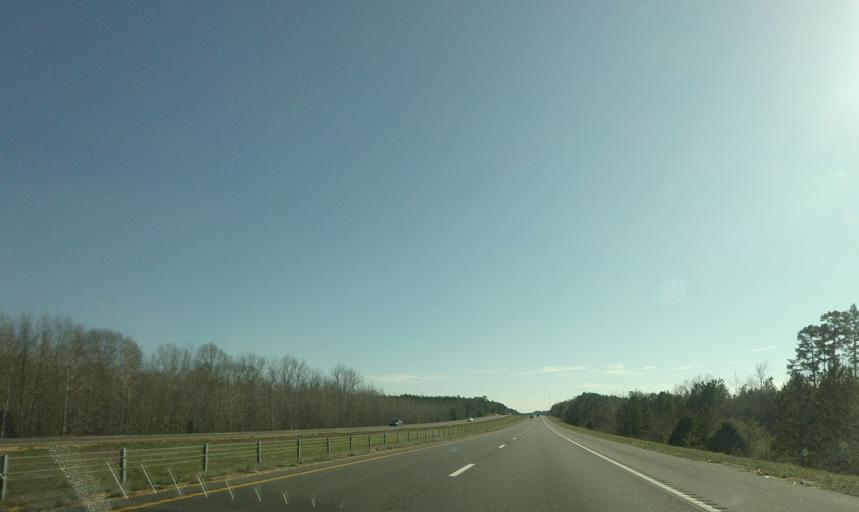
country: US
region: Mississippi
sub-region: Union County
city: New Albany
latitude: 34.5771
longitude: -89.1600
